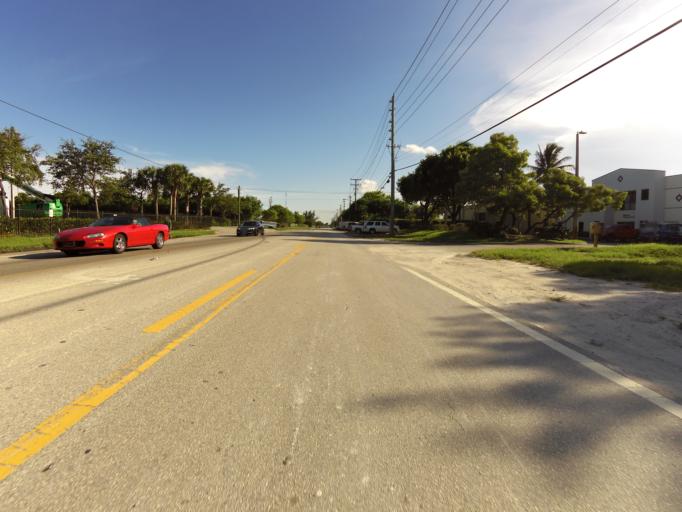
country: US
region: Florida
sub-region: Broward County
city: Broadview Park
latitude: 26.0932
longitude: -80.2345
